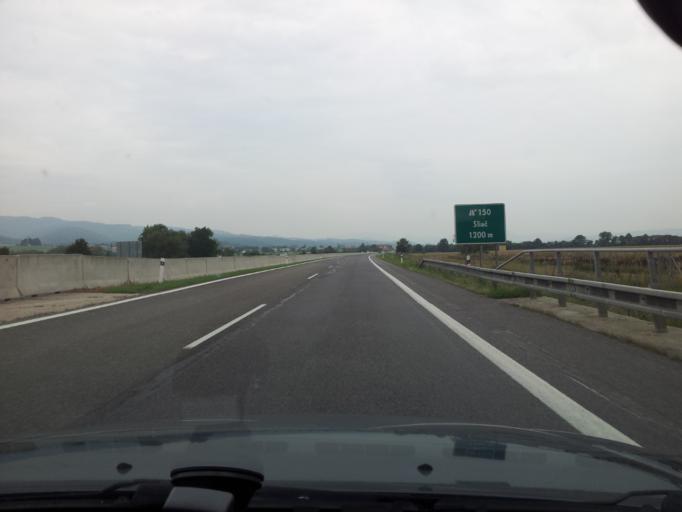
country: SK
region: Banskobystricky
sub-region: Okres Banska Bystrica
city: Zvolen
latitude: 48.6182
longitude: 19.1193
